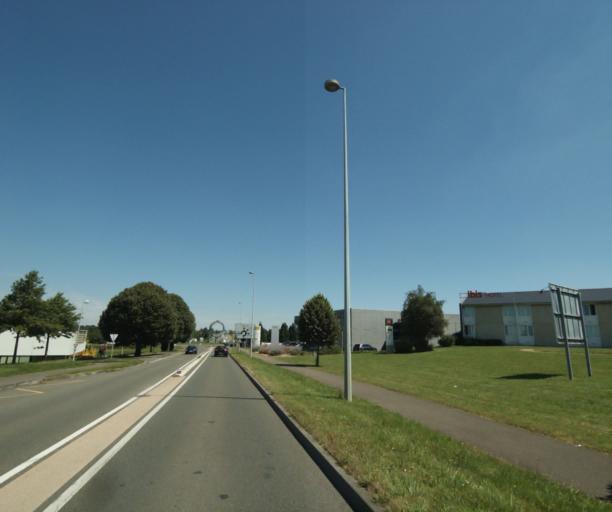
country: FR
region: Pays de la Loire
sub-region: Departement de la Mayenne
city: Laval
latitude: 48.0896
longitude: -0.7496
